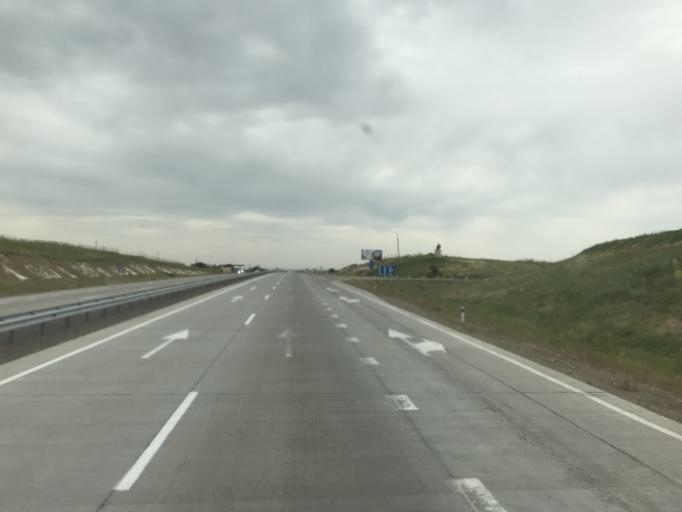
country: KZ
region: Ongtustik Qazaqstan
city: Qazyqurt
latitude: 41.6079
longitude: 69.4039
